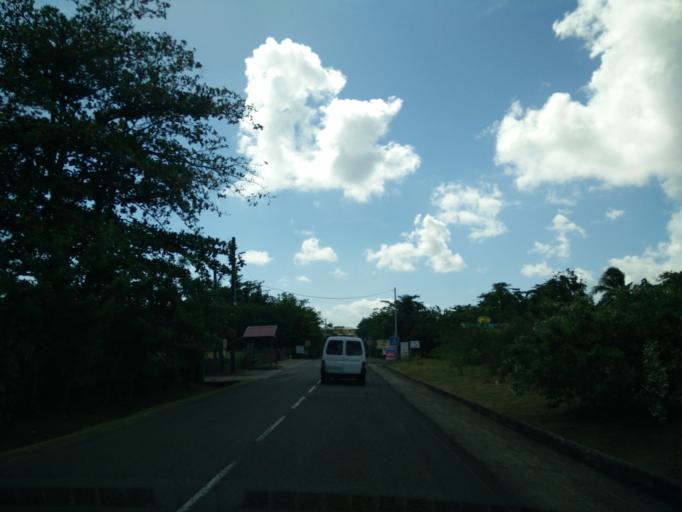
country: MQ
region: Martinique
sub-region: Martinique
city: Les Trois-Ilets
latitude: 14.5389
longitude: -61.0642
